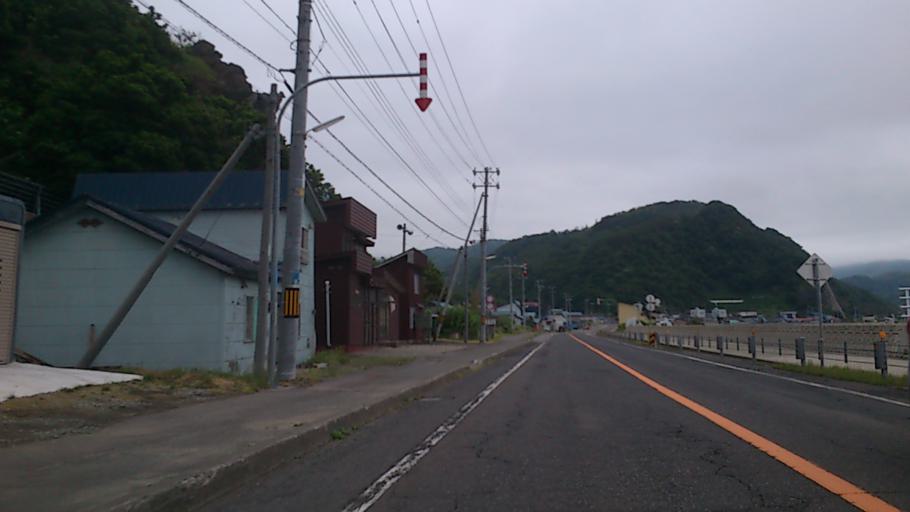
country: JP
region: Hokkaido
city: Iwanai
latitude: 42.7119
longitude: 140.0647
